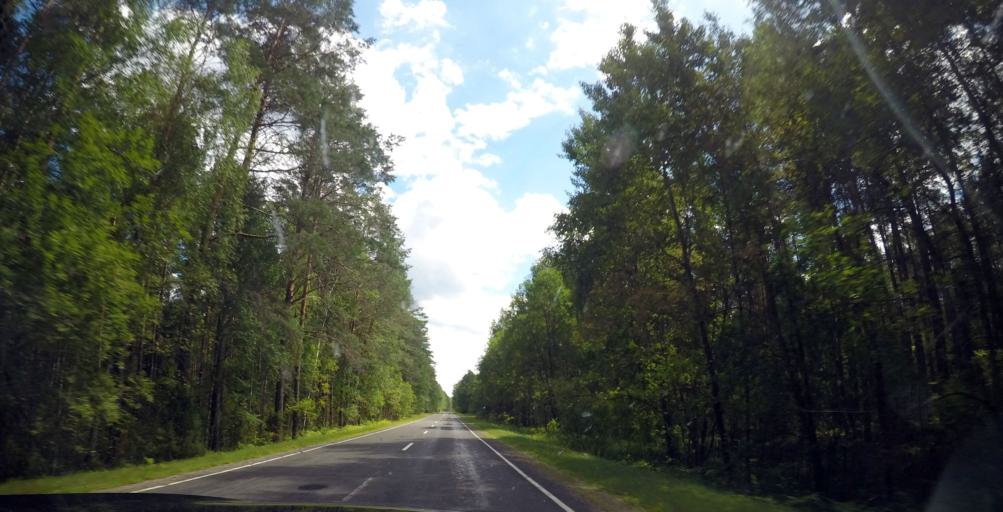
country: BY
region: Grodnenskaya
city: Skidal'
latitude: 53.8437
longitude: 24.2090
